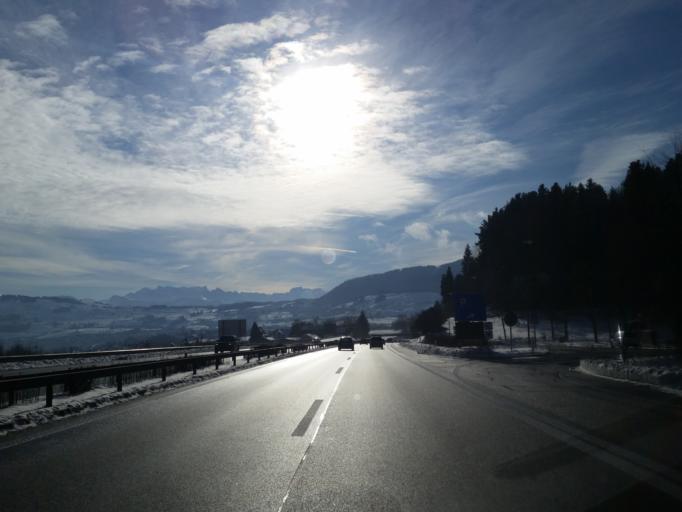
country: CH
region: Zurich
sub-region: Bezirk Horgen
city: Waedenswil / Eichweid
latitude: 47.2126
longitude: 8.6716
